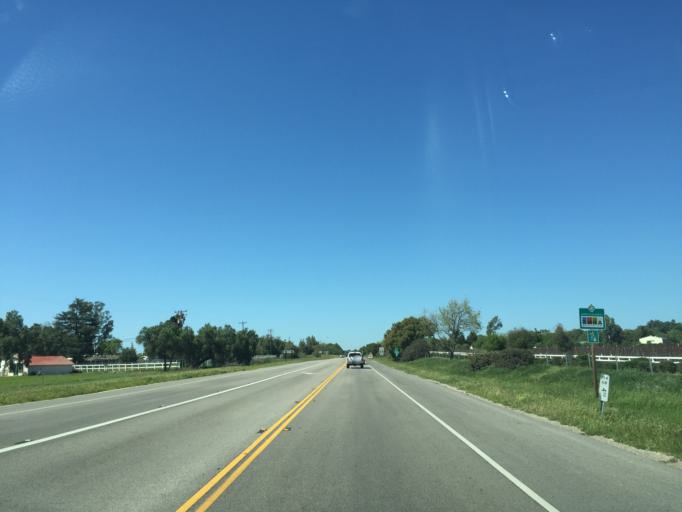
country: US
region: California
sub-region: Santa Barbara County
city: Los Olivos
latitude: 34.6508
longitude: -120.0955
